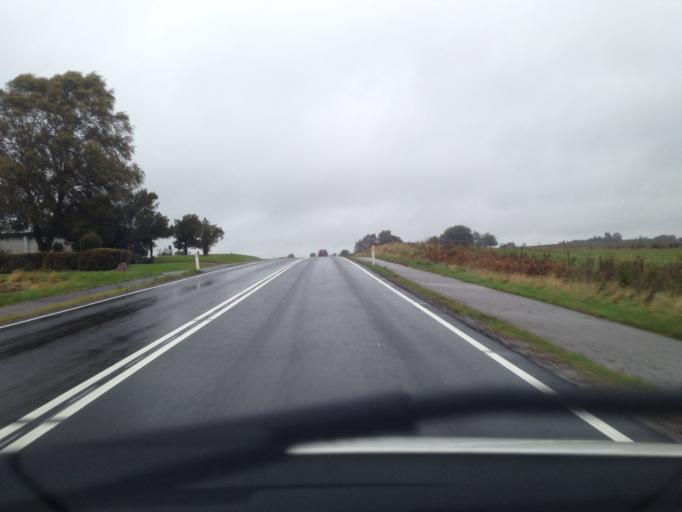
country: DK
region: Zealand
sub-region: Ringsted Kommune
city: Ringsted
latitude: 55.5178
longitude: 11.7292
